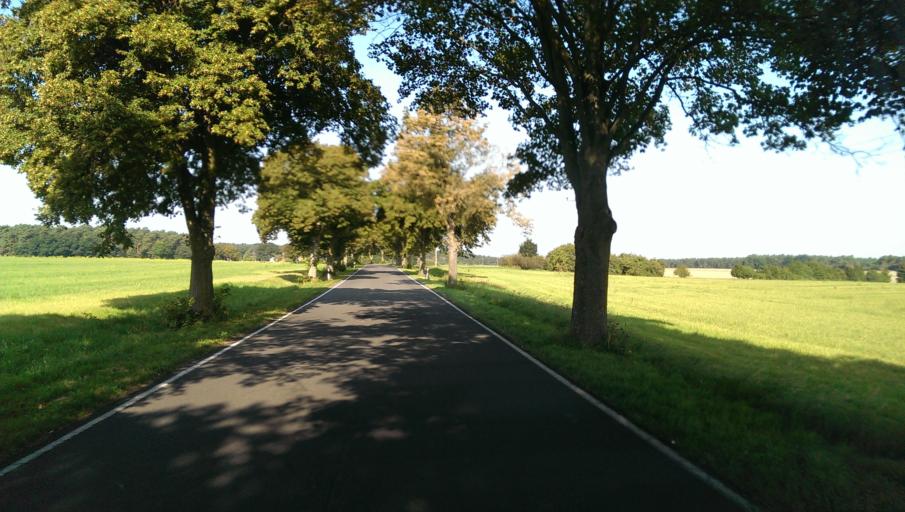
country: DE
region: Saxony-Anhalt
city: Kropstadt
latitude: 51.9795
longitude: 12.7184
